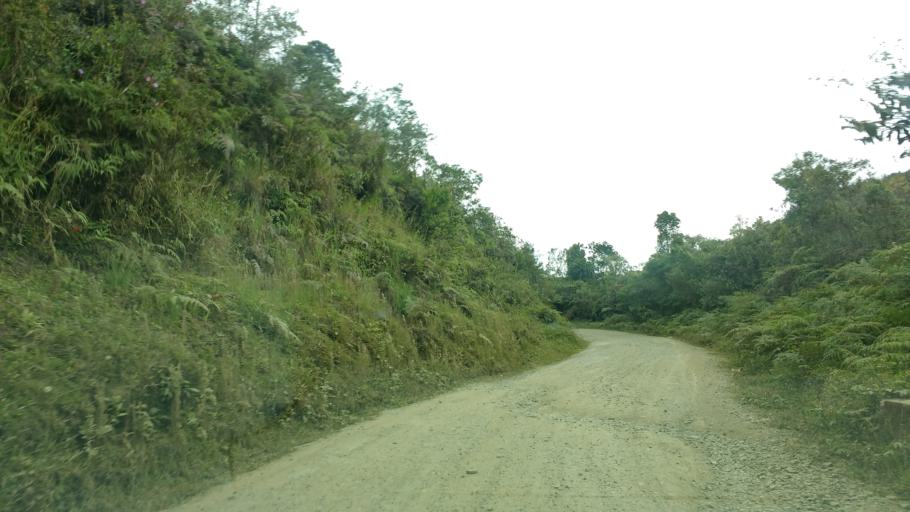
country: CO
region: Antioquia
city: Concepcion
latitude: 6.3395
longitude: -75.2759
